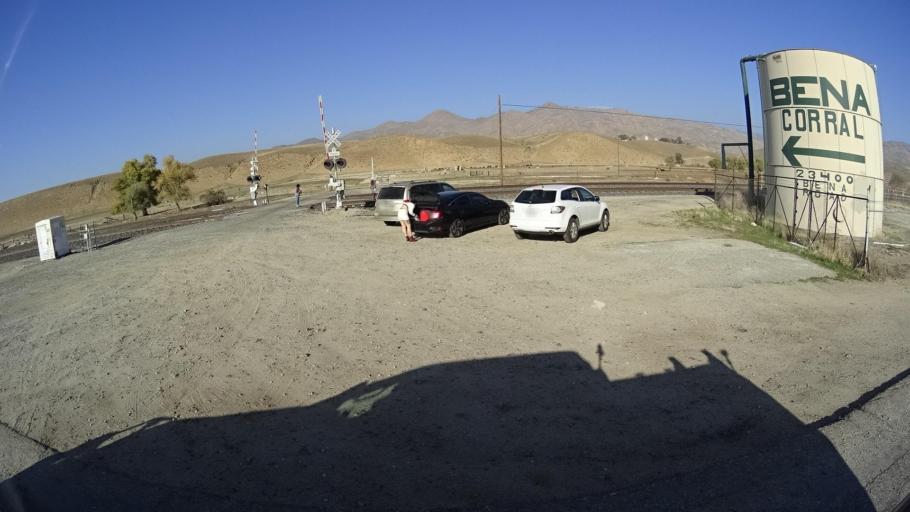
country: US
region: California
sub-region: Kern County
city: Arvin
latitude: 35.3266
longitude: -118.7412
